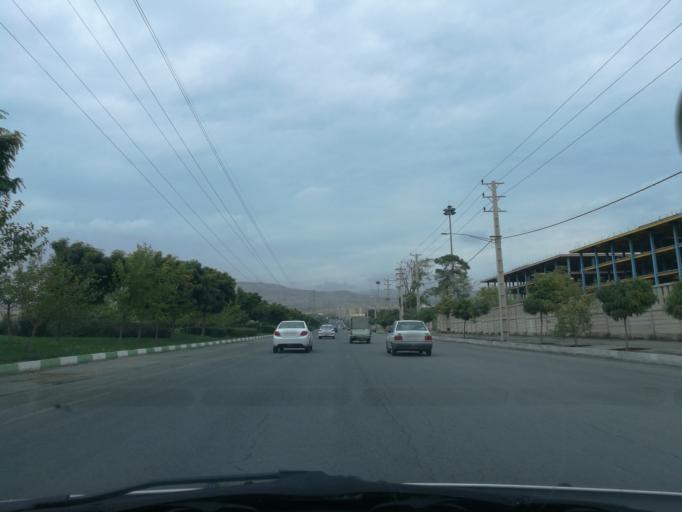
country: IR
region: Alborz
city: Karaj
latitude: 35.8568
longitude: 50.9221
